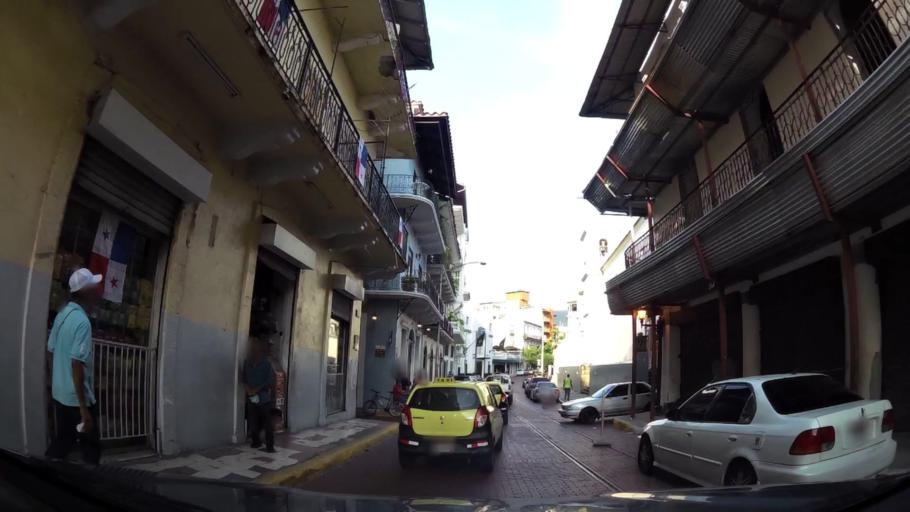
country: PA
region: Panama
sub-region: Distrito de Panama
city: Ancon
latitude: 8.9525
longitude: -79.5363
